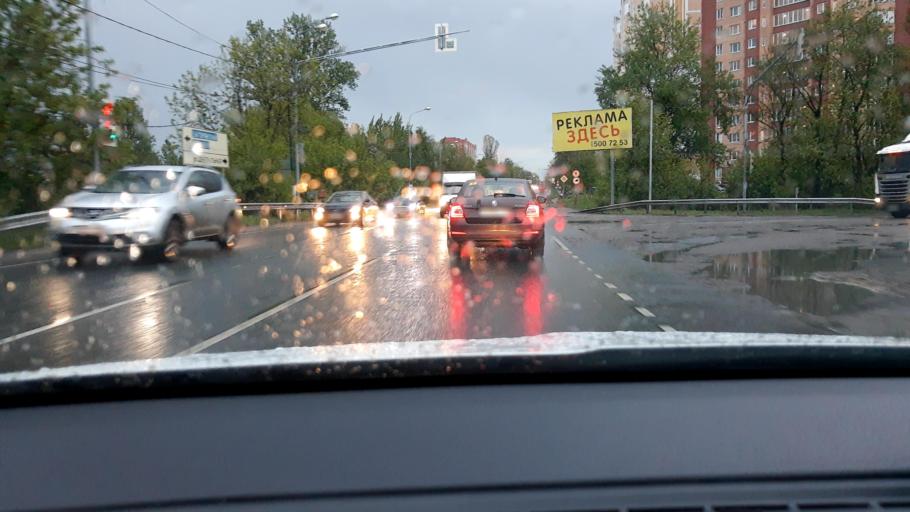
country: RU
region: Moskovskaya
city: Zagoryanskiy
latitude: 55.9282
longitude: 37.9545
